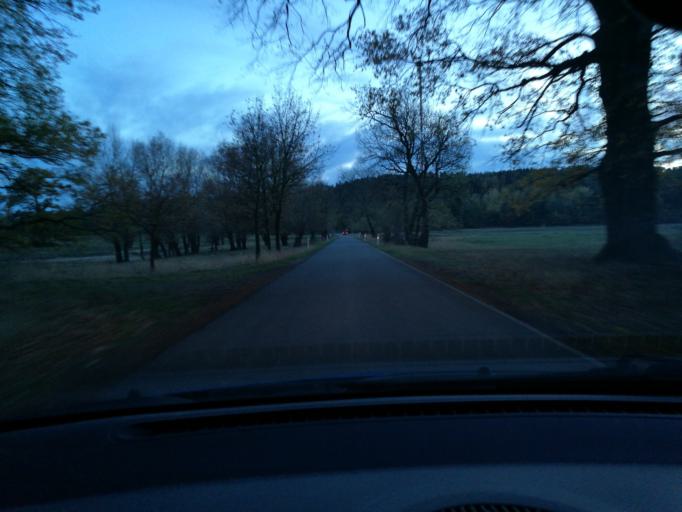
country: DE
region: Brandenburg
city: Lenzen
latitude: 53.0758
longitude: 11.4511
